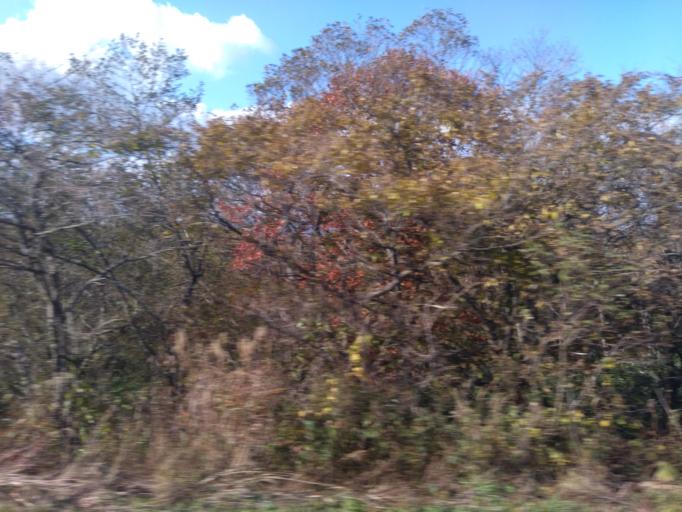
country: JP
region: Hokkaido
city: Shiraoi
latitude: 42.5313
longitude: 141.3221
